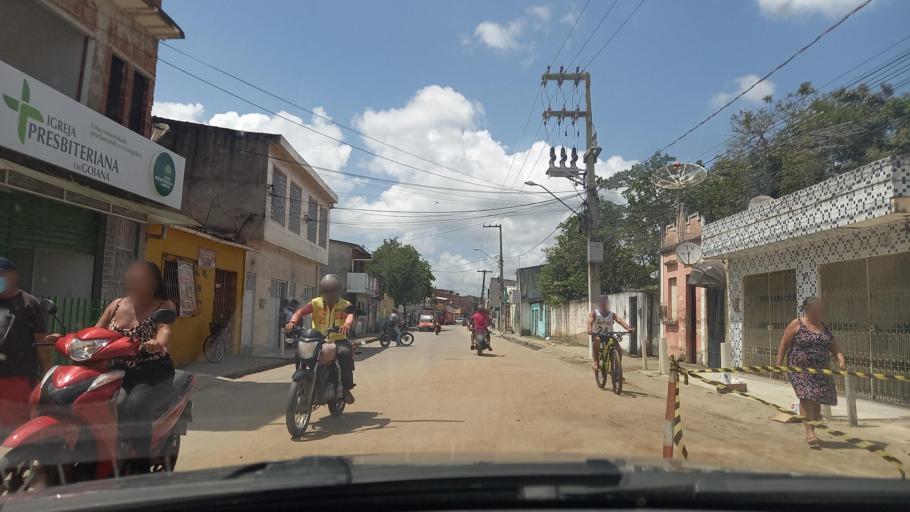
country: BR
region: Pernambuco
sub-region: Goiana
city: Goiana
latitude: -7.5609
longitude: -35.0080
